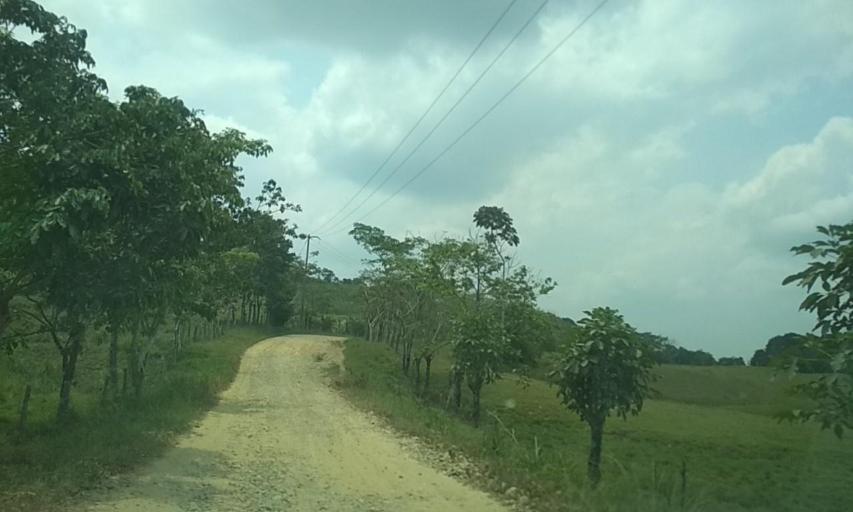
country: MX
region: Tabasco
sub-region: Huimanguillo
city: Francisco Rueda
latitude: 17.5868
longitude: -93.7912
